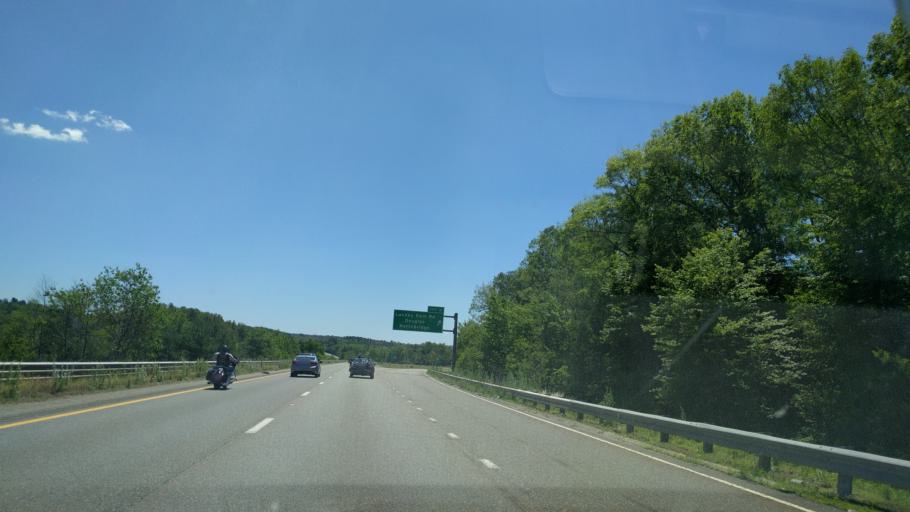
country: US
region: Massachusetts
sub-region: Worcester County
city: East Douglas
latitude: 42.0922
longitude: -71.6977
